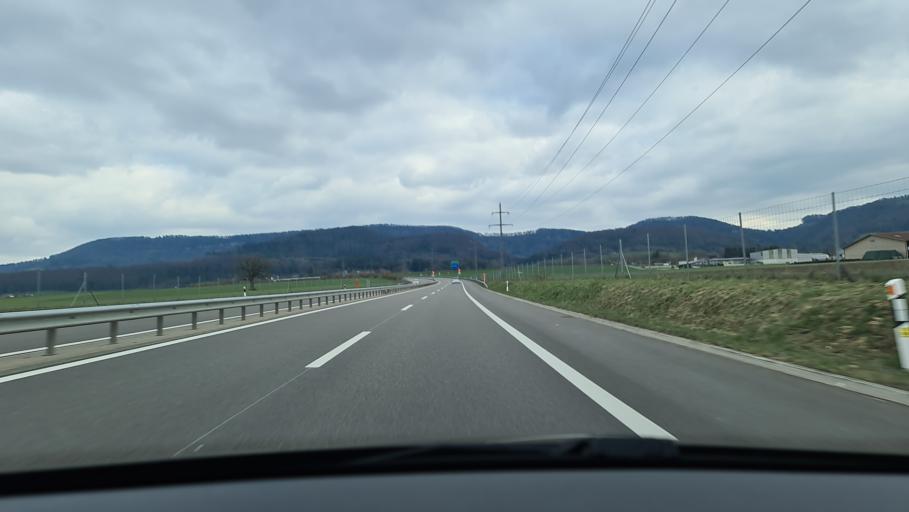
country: CH
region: Jura
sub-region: Porrentruy District
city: Courgenay
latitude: 47.4127
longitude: 7.1345
